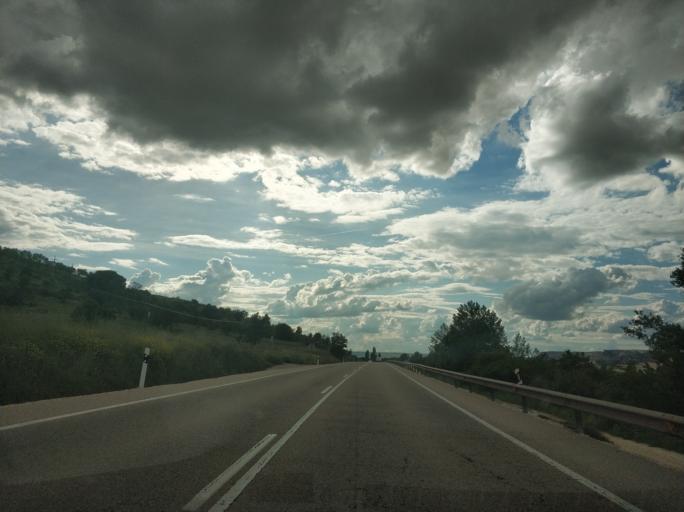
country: ES
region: Castille and Leon
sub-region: Provincia de Valladolid
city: Bocos de Duero
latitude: 41.6106
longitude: -4.0844
